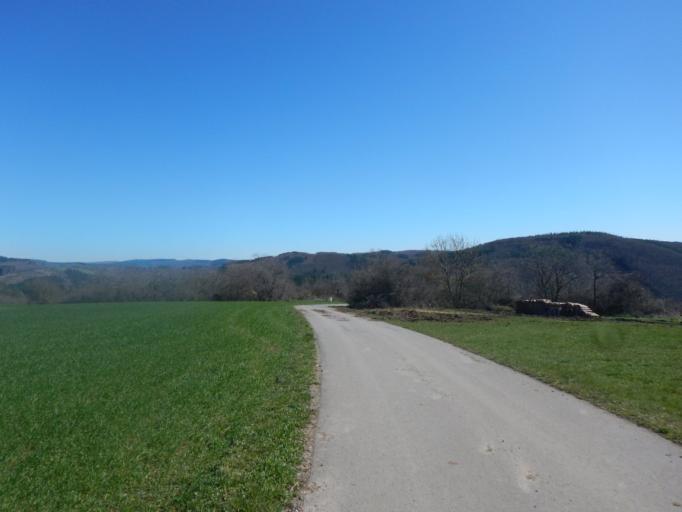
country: LU
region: Diekirch
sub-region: Canton de Wiltz
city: Eschweiler
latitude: 49.9836
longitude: 5.9500
